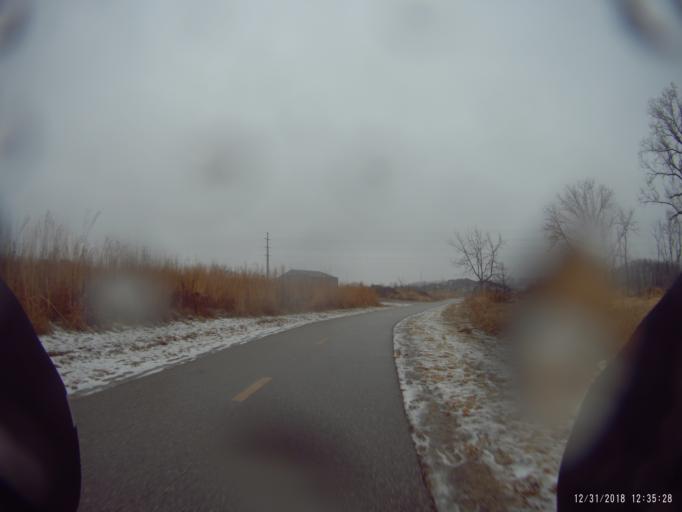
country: US
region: Wisconsin
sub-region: Dane County
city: Verona
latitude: 43.0149
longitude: -89.5190
